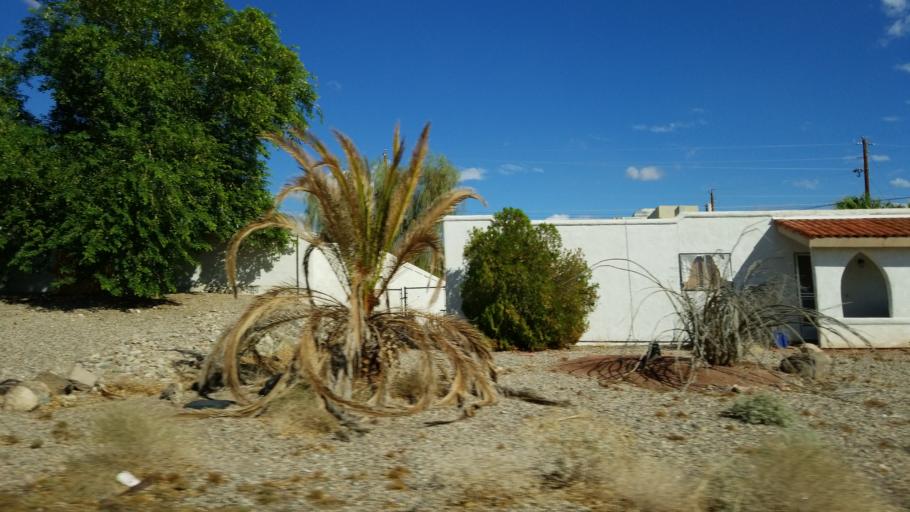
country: US
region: Arizona
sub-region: Mohave County
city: Lake Havasu City
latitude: 34.4796
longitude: -114.2672
